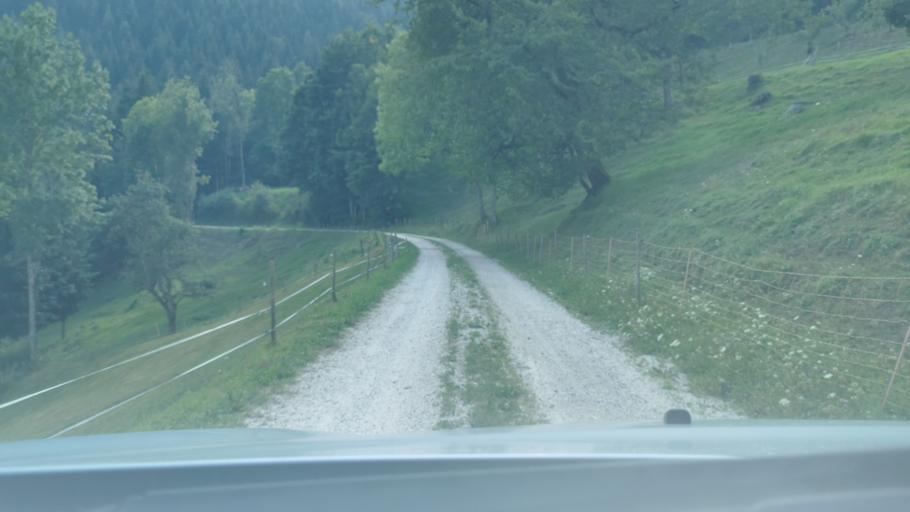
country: AT
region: Styria
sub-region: Politischer Bezirk Weiz
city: Fischbach
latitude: 47.4071
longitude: 15.6334
